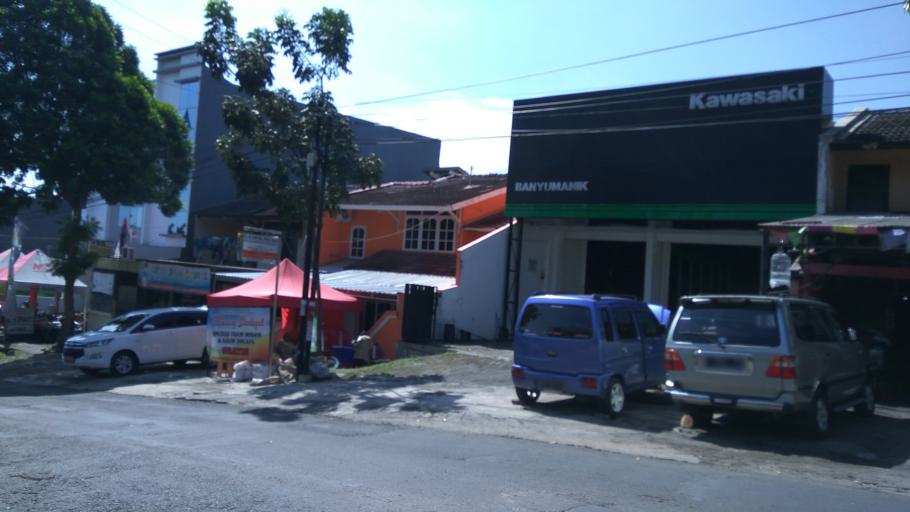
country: ID
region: Central Java
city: Ungaran
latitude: -7.0698
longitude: 110.4202
